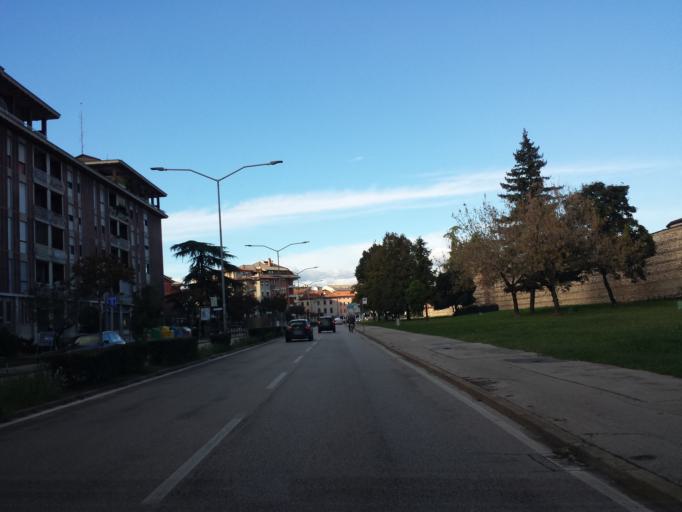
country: IT
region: Veneto
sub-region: Provincia di Vicenza
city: Vicenza
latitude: 45.5503
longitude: 11.5352
